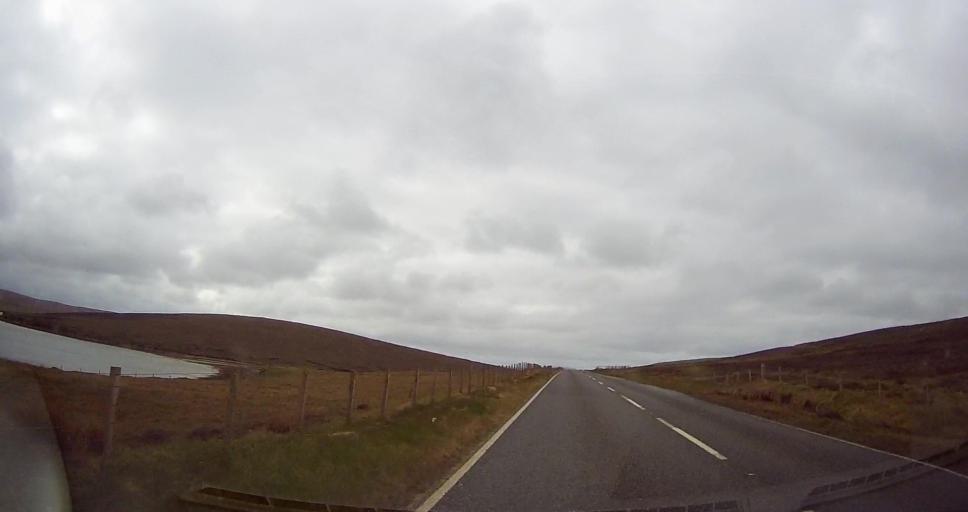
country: GB
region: Scotland
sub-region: Shetland Islands
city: Lerwick
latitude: 60.2499
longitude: -1.3747
